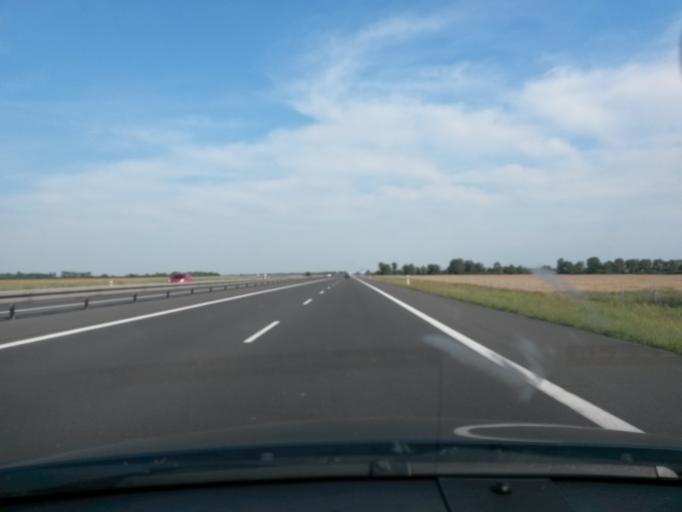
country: PL
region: Greater Poland Voivodeship
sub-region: Powiat wrzesinski
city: Wrzesnia
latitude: 52.3031
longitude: 17.6144
